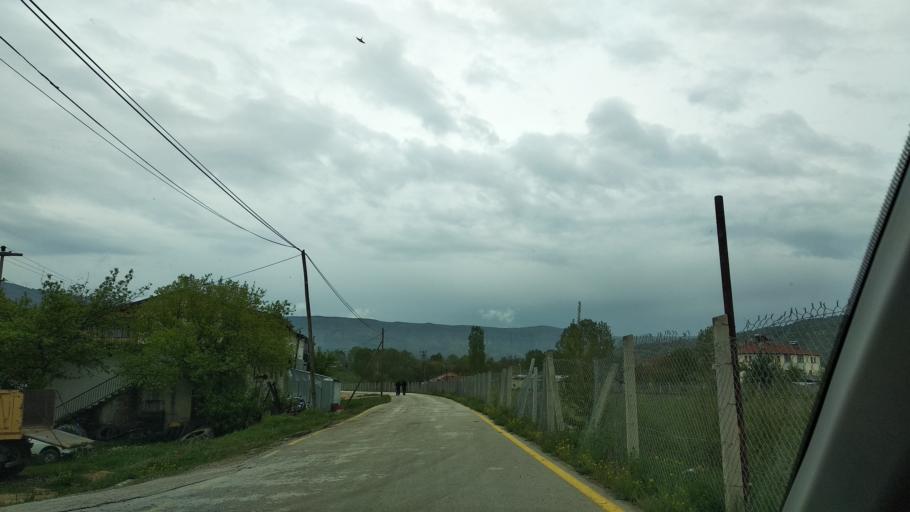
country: TR
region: Bolu
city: Seben
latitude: 40.4072
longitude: 31.5703
